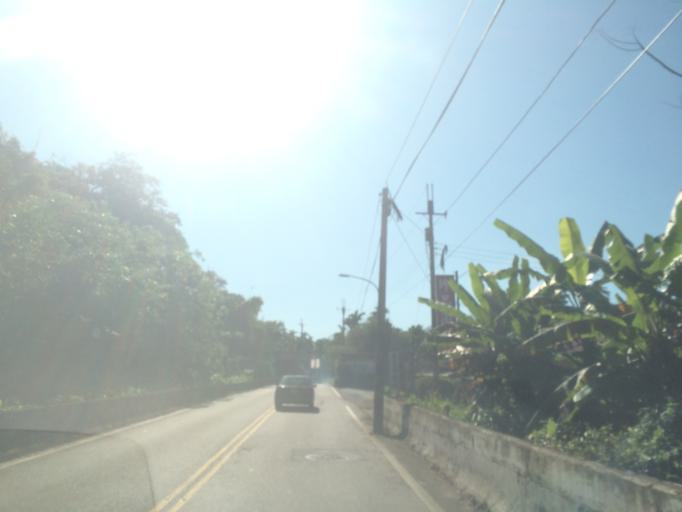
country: TW
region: Taiwan
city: Lugu
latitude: 23.7219
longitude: 120.7780
